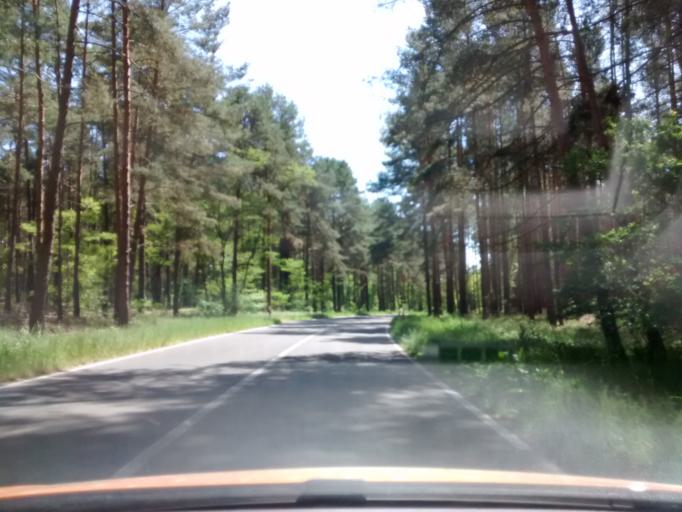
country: DE
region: Brandenburg
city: Wendisch Rietz
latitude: 52.2263
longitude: 13.9995
